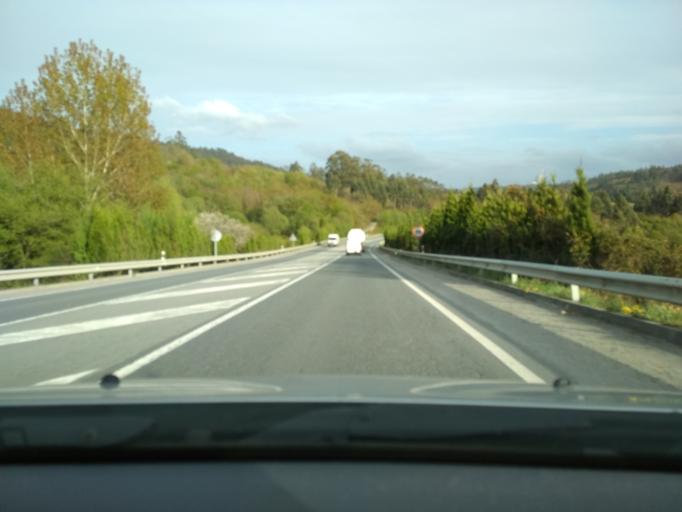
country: ES
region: Galicia
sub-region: Provincia da Coruna
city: Cerceda
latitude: 43.2253
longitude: -8.4616
